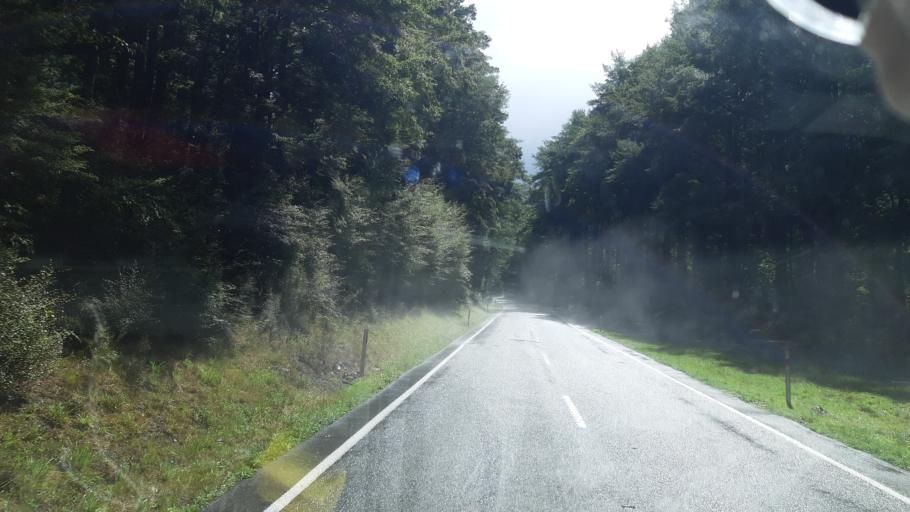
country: NZ
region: Canterbury
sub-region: Hurunui District
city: Amberley
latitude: -42.3786
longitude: 172.2773
